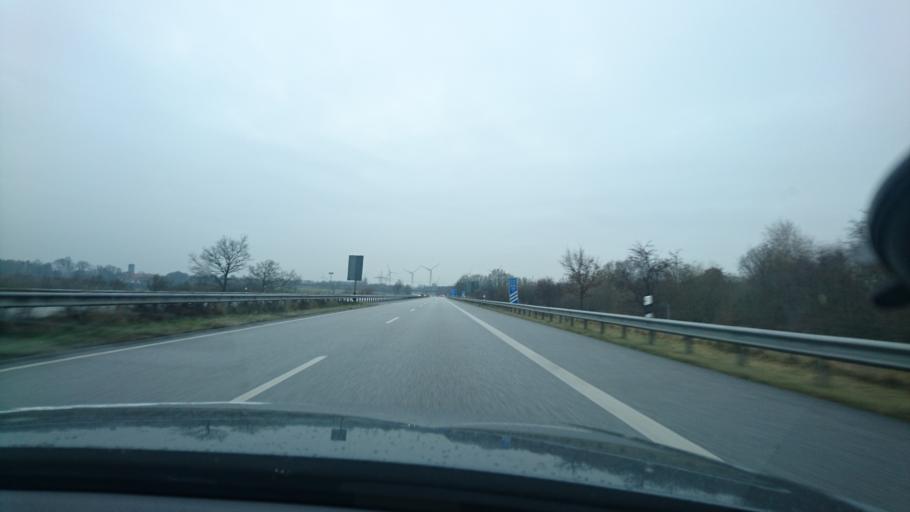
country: DE
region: Schleswig-Holstein
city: Kabelhorst
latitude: 54.2087
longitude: 10.9006
